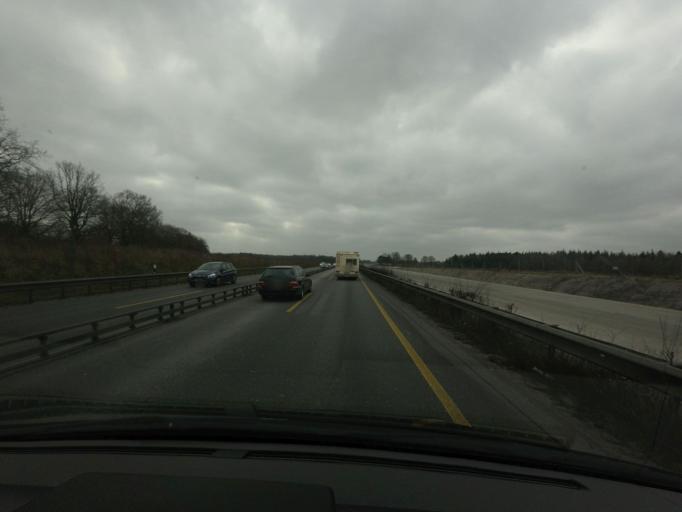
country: DE
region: Schleswig-Holstein
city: Bonningstedt
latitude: 53.6757
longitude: 9.9430
